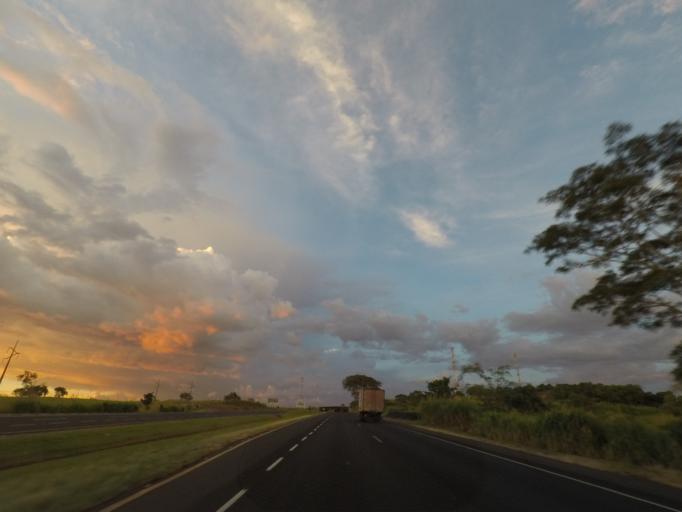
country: BR
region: Minas Gerais
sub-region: Uberaba
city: Uberaba
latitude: -19.5892
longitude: -48.0293
